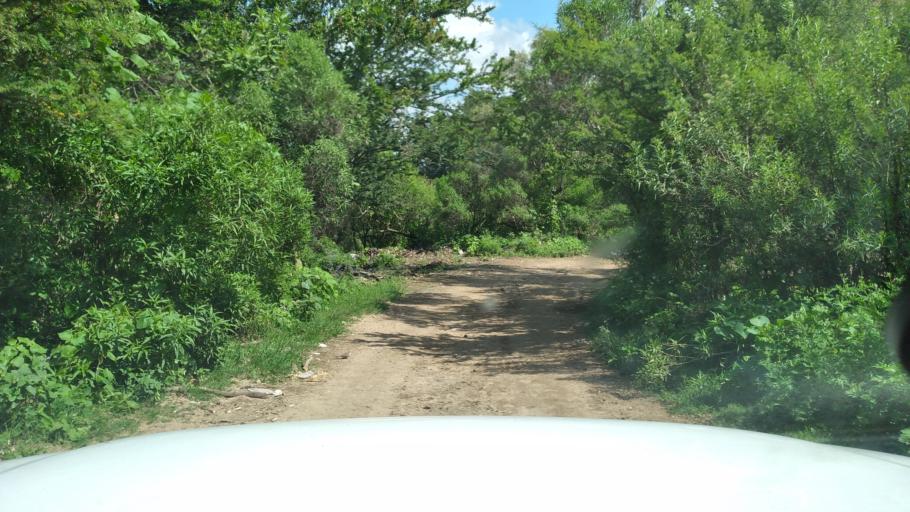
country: MX
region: Jalisco
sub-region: Zapopan
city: San Isidro
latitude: 20.7289
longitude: -103.2970
